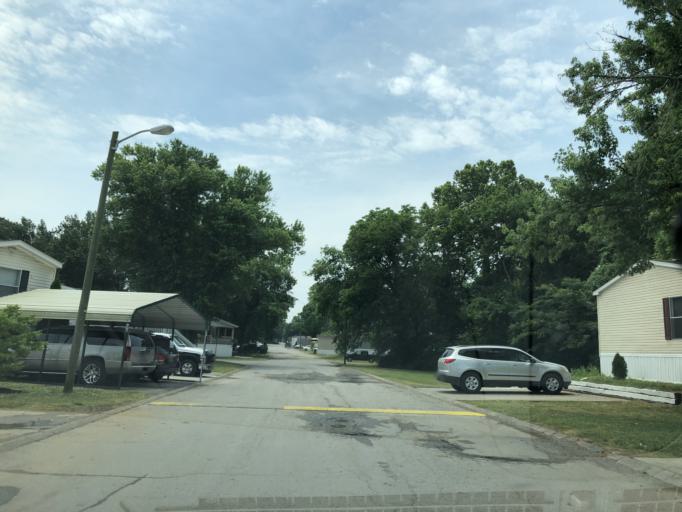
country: US
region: Tennessee
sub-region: Davidson County
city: Oak Hill
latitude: 36.0737
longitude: -86.6786
